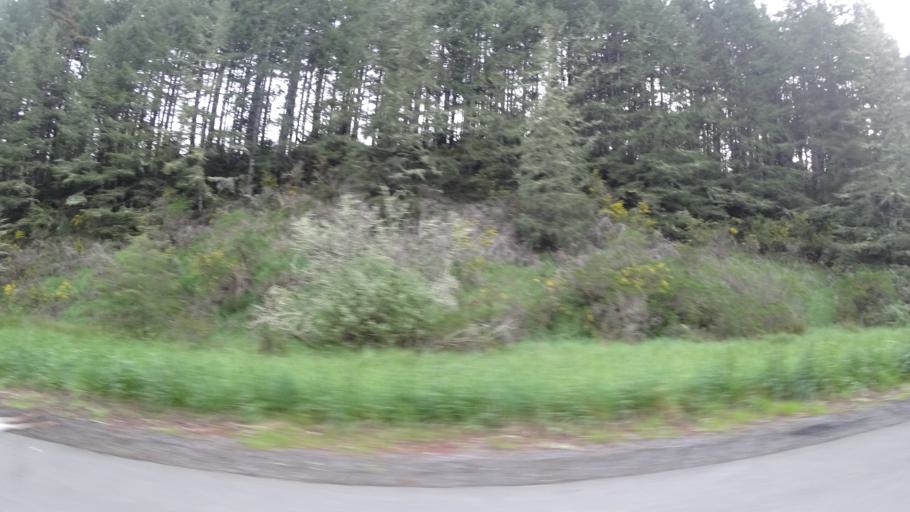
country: US
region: Oregon
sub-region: Coos County
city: Bandon
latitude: 43.1917
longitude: -124.3423
